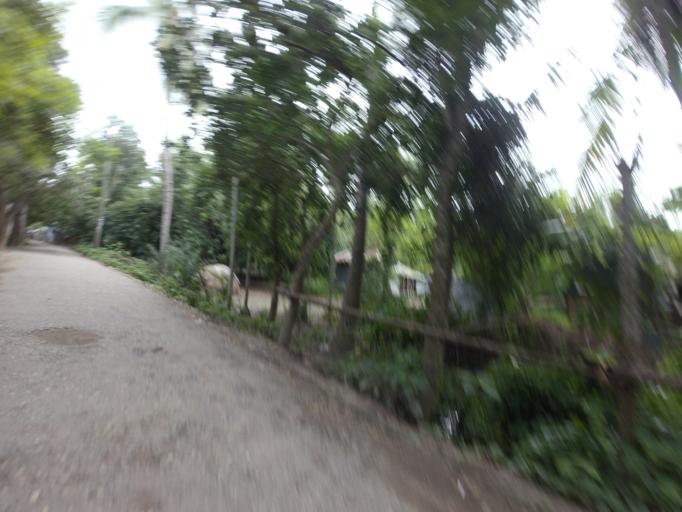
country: BD
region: Khulna
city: Kalia
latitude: 23.0486
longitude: 89.6461
